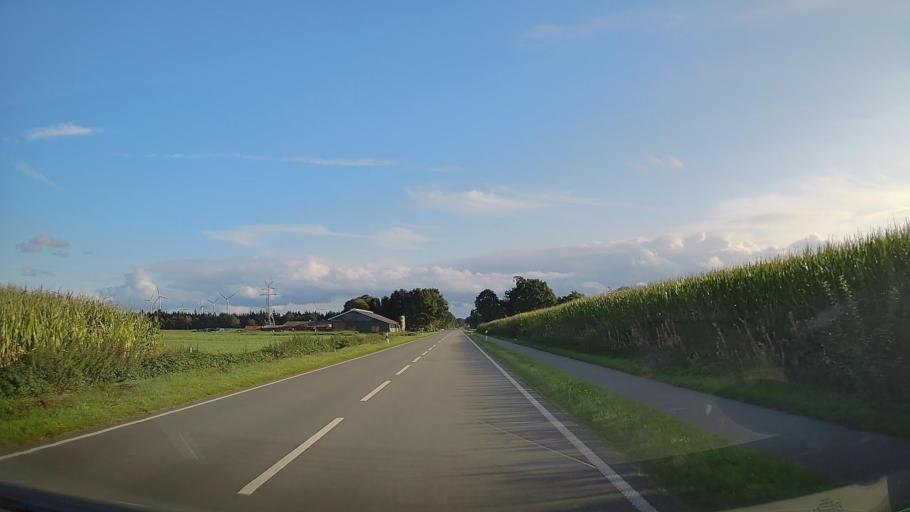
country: DE
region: Lower Saxony
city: Barssel
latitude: 53.1041
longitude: 7.7092
